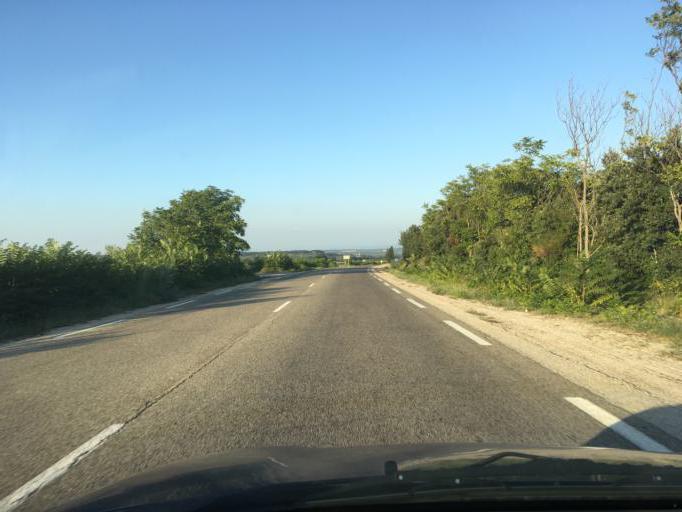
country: FR
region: Languedoc-Roussillon
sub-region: Departement du Gard
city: Tavel
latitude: 44.0172
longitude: 4.7336
